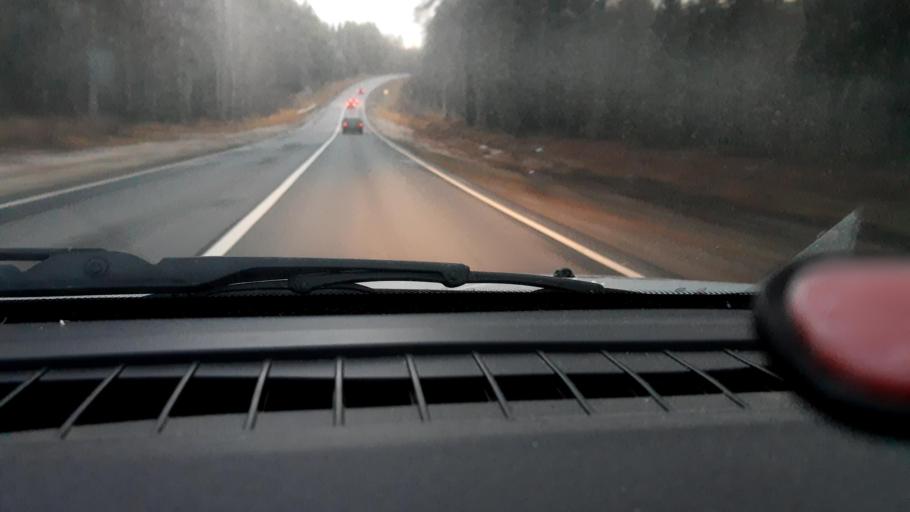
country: RU
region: Nizjnij Novgorod
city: Krasnyye Baki
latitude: 56.9897
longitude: 45.1165
